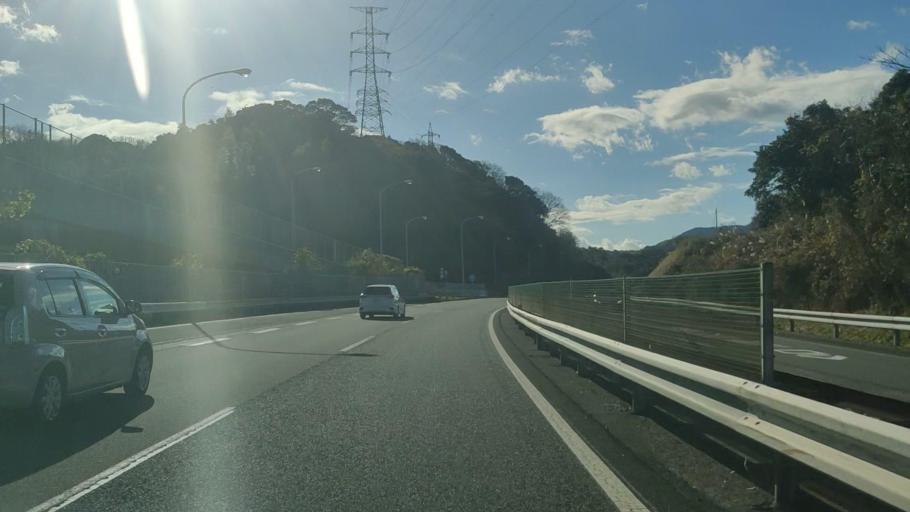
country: JP
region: Fukuoka
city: Kitakyushu
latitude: 33.8592
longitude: 130.8469
